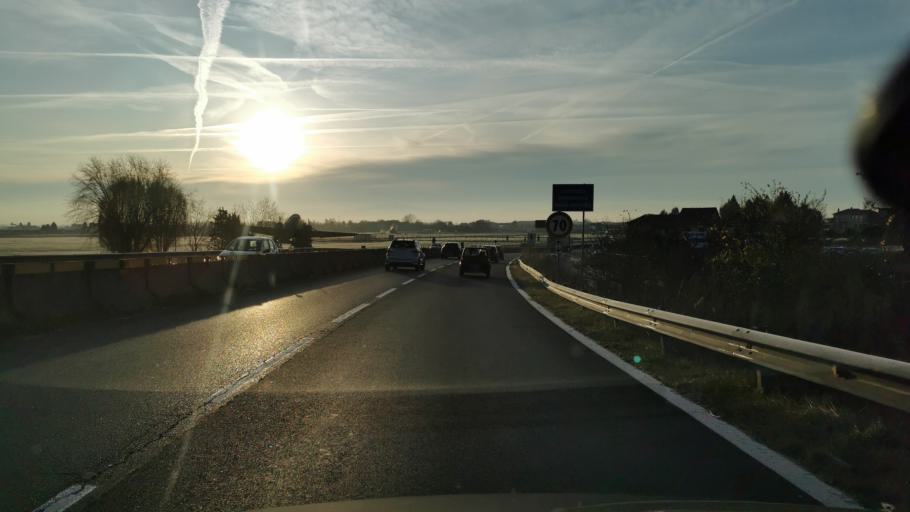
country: IT
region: Piedmont
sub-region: Provincia di Torino
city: Caselle Torinese
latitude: 45.1863
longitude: 7.6440
